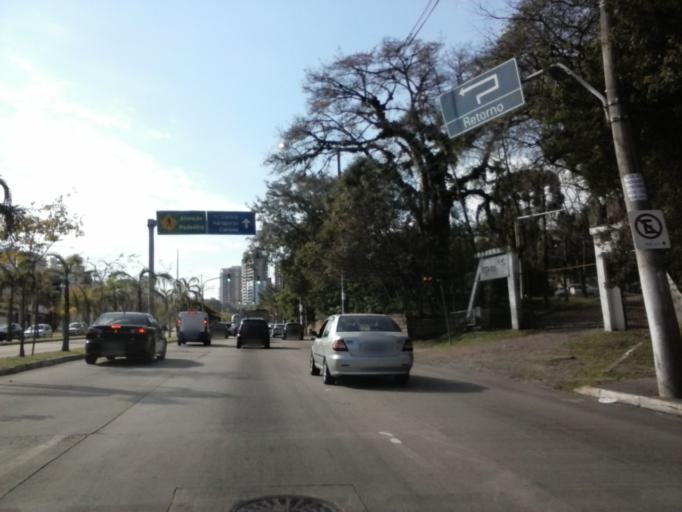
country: BR
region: Rio Grande do Sul
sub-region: Porto Alegre
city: Porto Alegre
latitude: -30.0489
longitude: -51.1790
